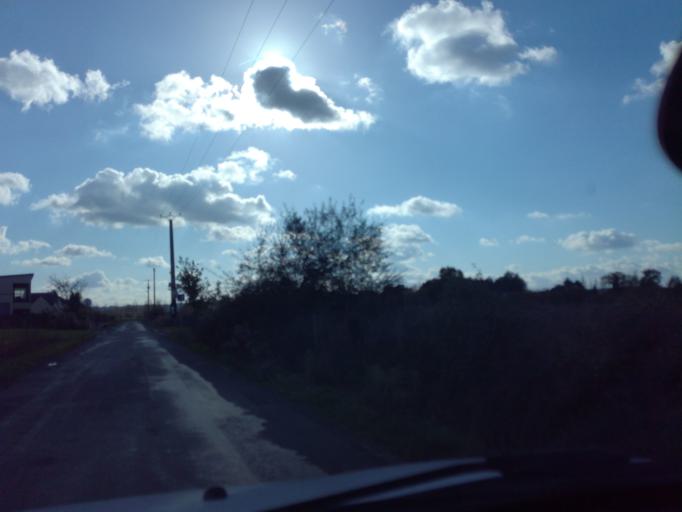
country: FR
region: Brittany
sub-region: Departement d'Ille-et-Vilaine
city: Chavagne
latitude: 48.0523
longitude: -1.8008
